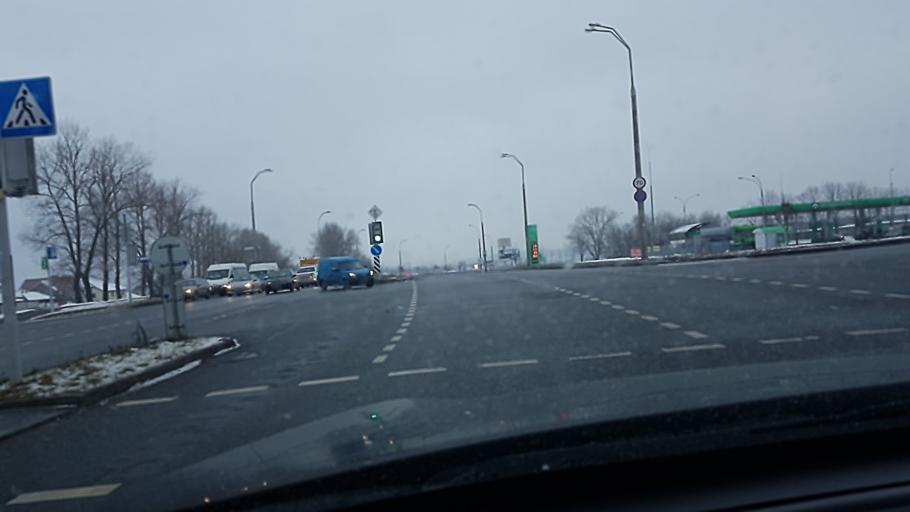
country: BY
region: Minsk
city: Bal'shavik
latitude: 53.9595
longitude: 27.5366
